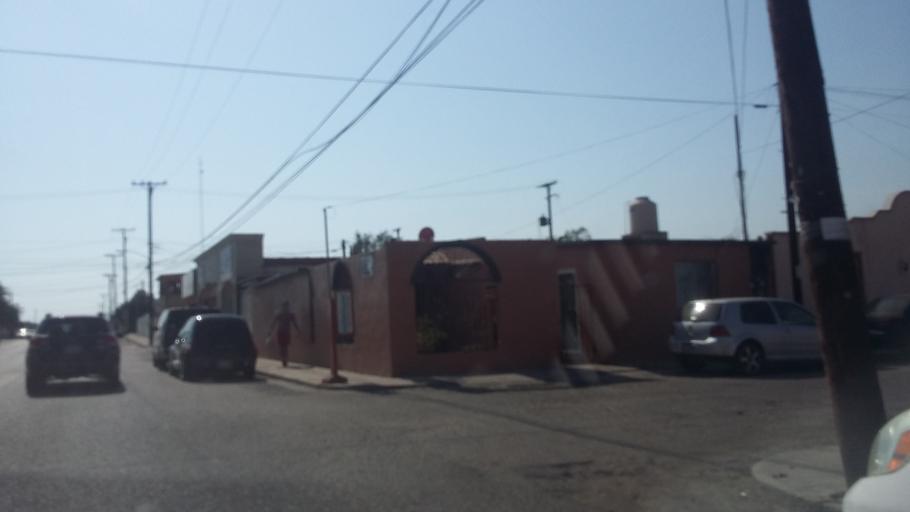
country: MX
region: Baja California
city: Ensenada
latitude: 31.8303
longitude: -116.6016
